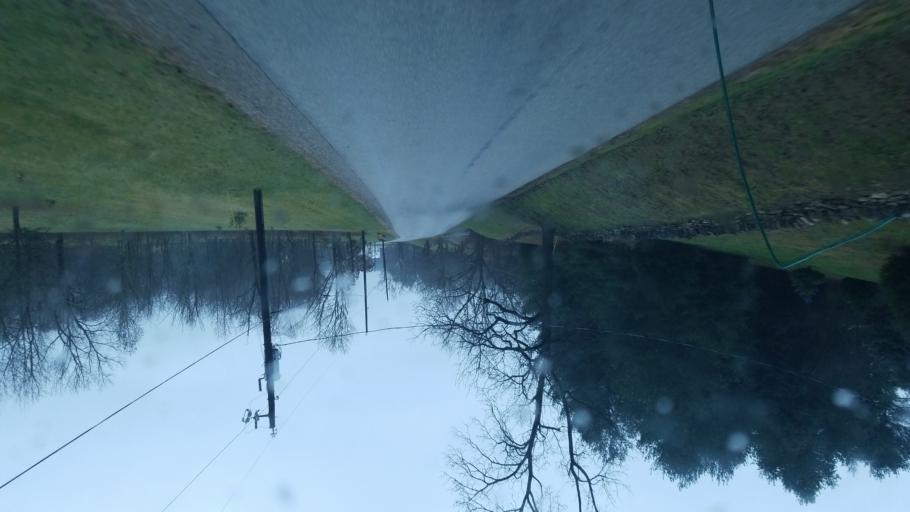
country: US
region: Ohio
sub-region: Delaware County
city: Powell
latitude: 40.1795
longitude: -83.0455
